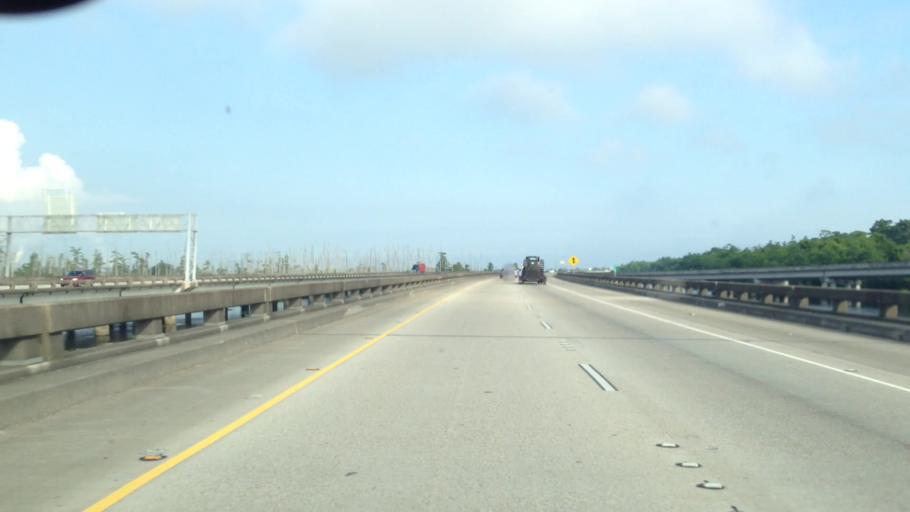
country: US
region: Louisiana
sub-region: Saint Charles Parish
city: Ama
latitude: 30.0078
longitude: -90.2969
